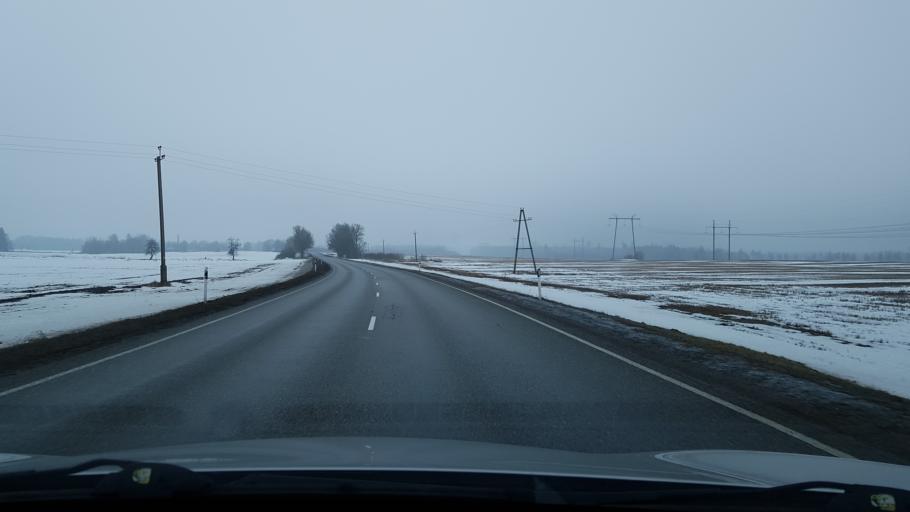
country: EE
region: Valgamaa
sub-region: Valga linn
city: Valga
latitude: 57.9405
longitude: 26.1686
